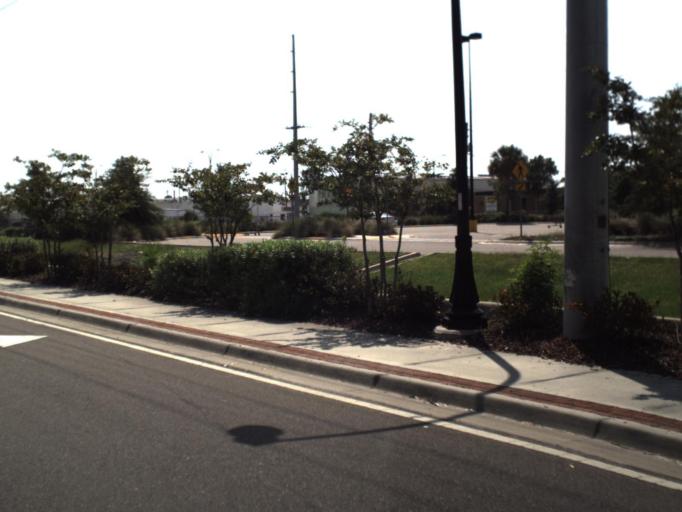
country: US
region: Florida
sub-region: Hillsborough County
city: Tampa
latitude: 27.8937
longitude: -82.5163
